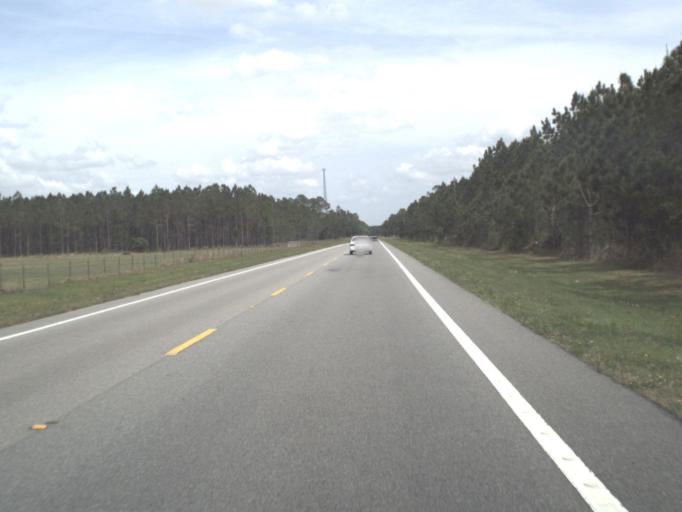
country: US
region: Florida
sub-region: Putnam County
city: Crescent City
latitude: 29.4892
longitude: -81.4687
